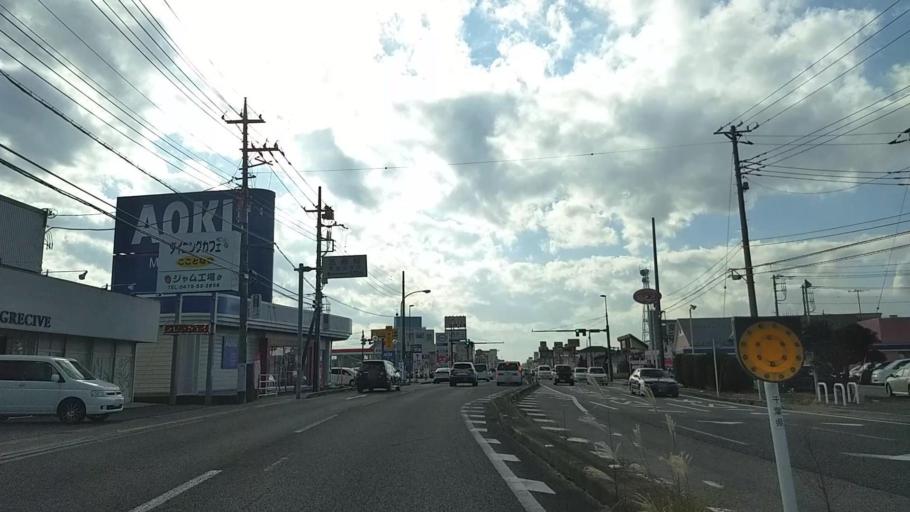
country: JP
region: Chiba
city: Togane
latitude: 35.5610
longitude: 140.3730
